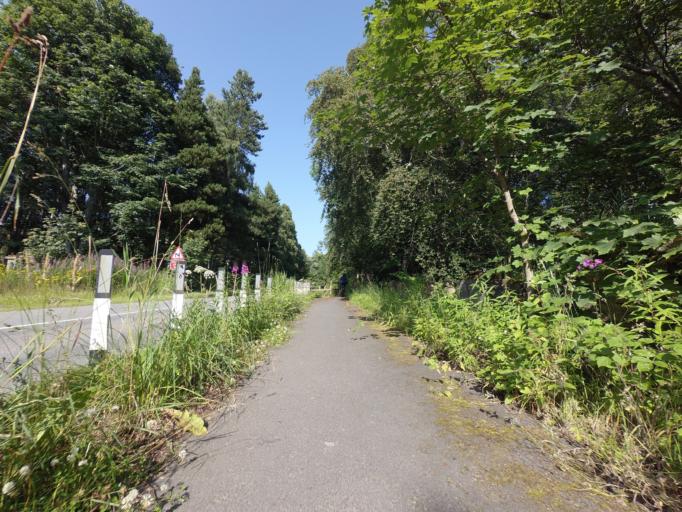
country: GB
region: Scotland
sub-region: Highland
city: Evanton
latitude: 57.6756
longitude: -4.3144
